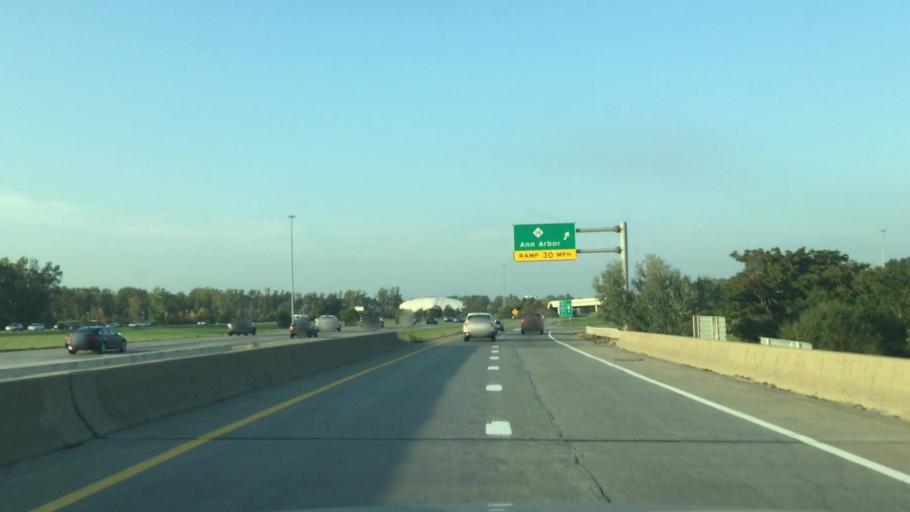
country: US
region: Michigan
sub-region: Wayne County
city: Plymouth
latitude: 42.3800
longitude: -83.4468
